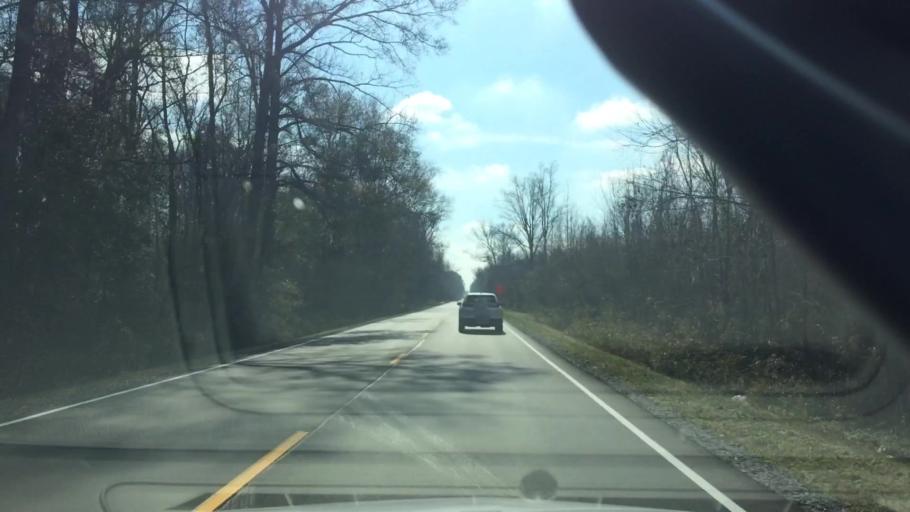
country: US
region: North Carolina
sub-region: Duplin County
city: Beulaville
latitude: 34.9484
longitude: -77.7676
